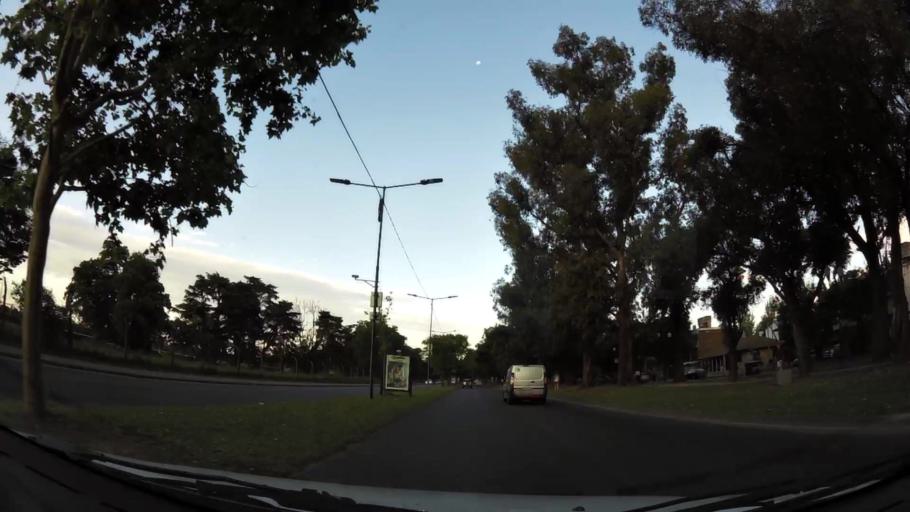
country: AR
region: Buenos Aires
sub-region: Partido de San Isidro
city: San Isidro
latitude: -34.4845
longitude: -58.5151
